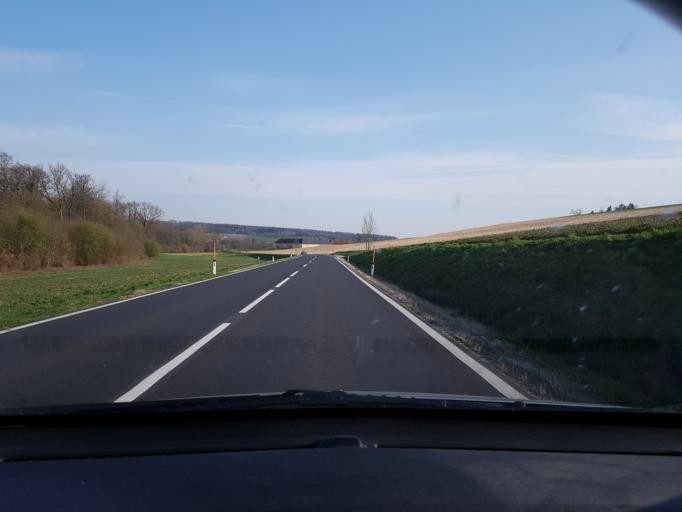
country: AT
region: Upper Austria
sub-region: Politischer Bezirk Linz-Land
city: Sankt Florian
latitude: 48.1822
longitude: 14.3454
